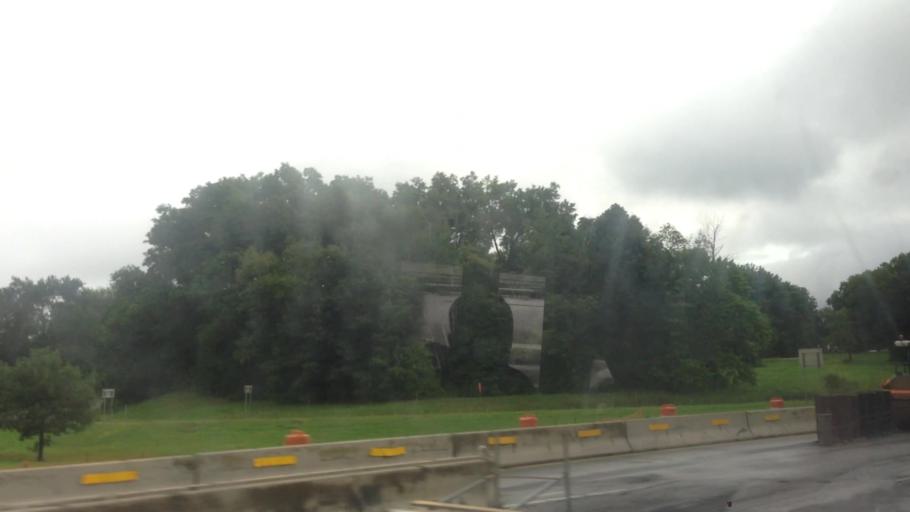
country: US
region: New York
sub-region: Ulster County
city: Lake Katrine
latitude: 41.9760
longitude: -74.0023
